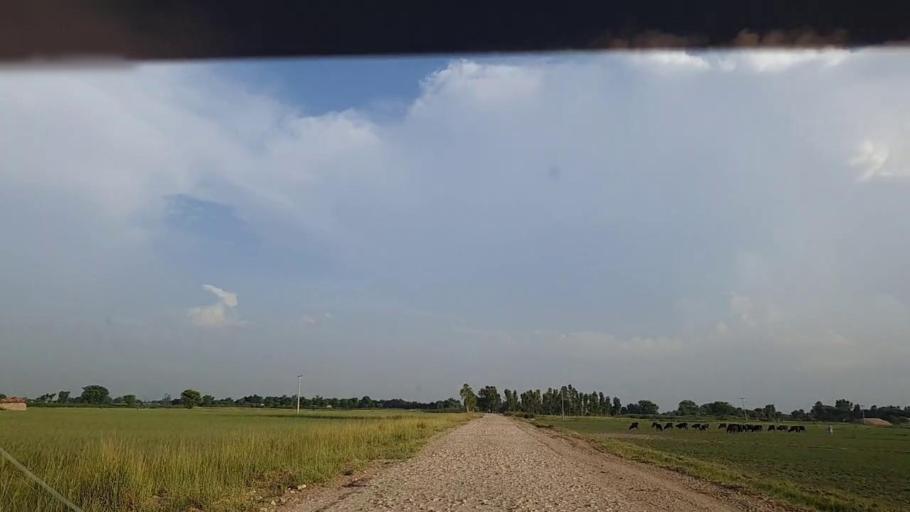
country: PK
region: Sindh
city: Khanpur
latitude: 27.8123
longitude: 69.3370
